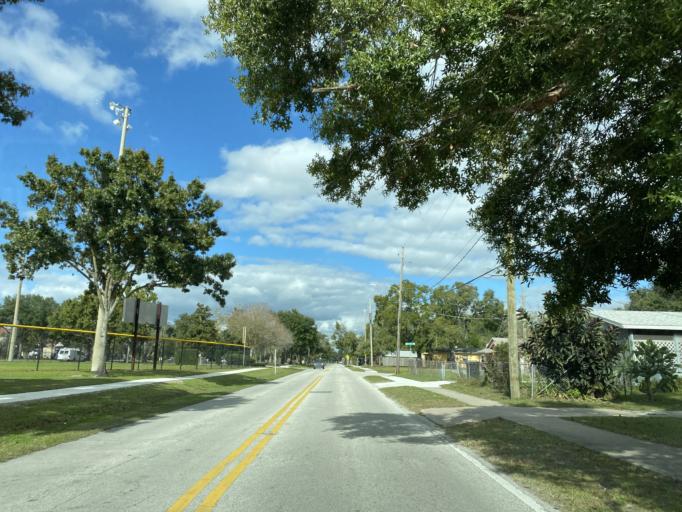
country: US
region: Florida
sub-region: Orange County
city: Orlando
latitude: 28.5241
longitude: -81.3888
